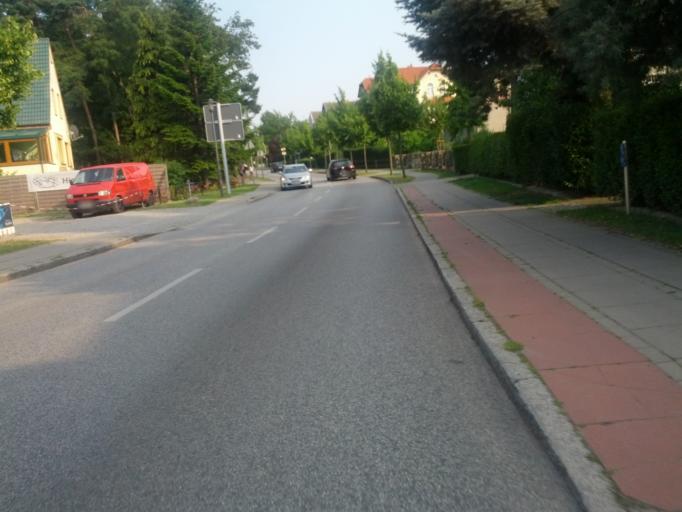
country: DE
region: Mecklenburg-Vorpommern
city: Ostseebad Kuhlungsborn
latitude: 54.1477
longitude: 11.7304
